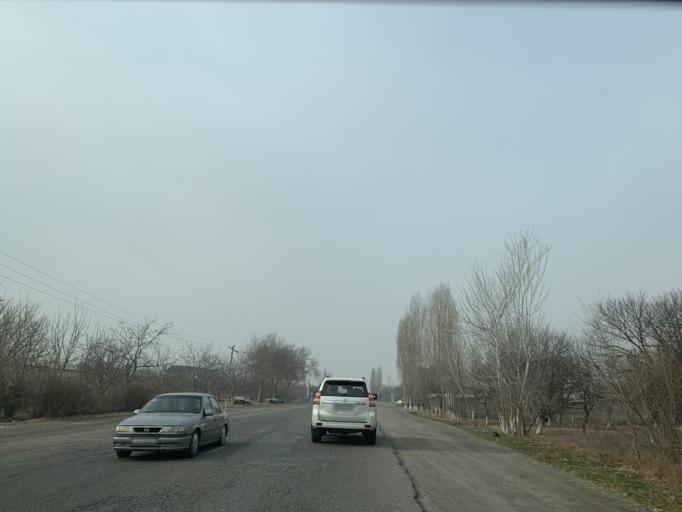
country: TJ
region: Viloyati Sughd
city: Ghafurov
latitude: 40.1946
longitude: 69.8481
